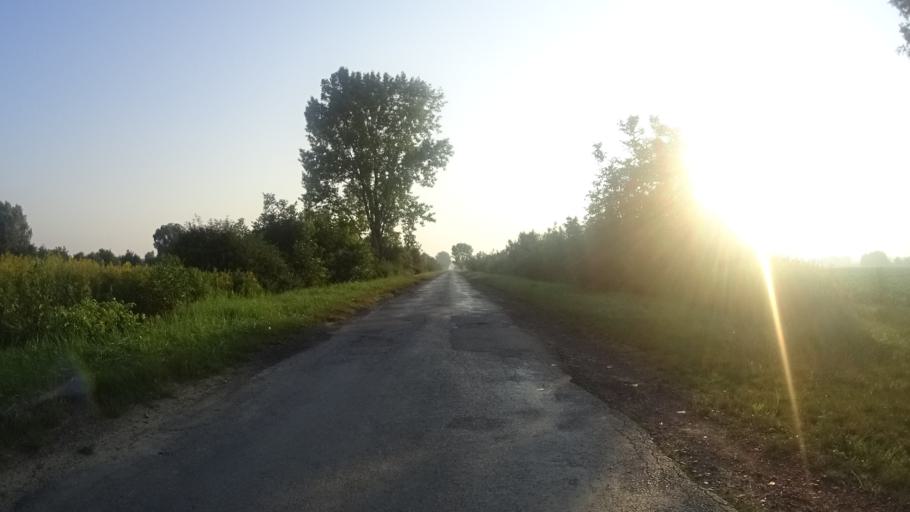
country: HU
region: Zala
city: Zalakomar
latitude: 46.5342
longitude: 17.1446
